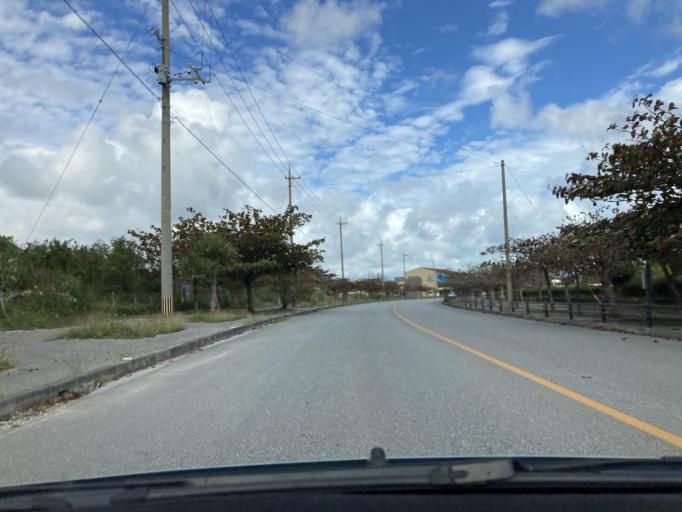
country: JP
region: Okinawa
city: Ginowan
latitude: 26.2102
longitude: 127.7674
